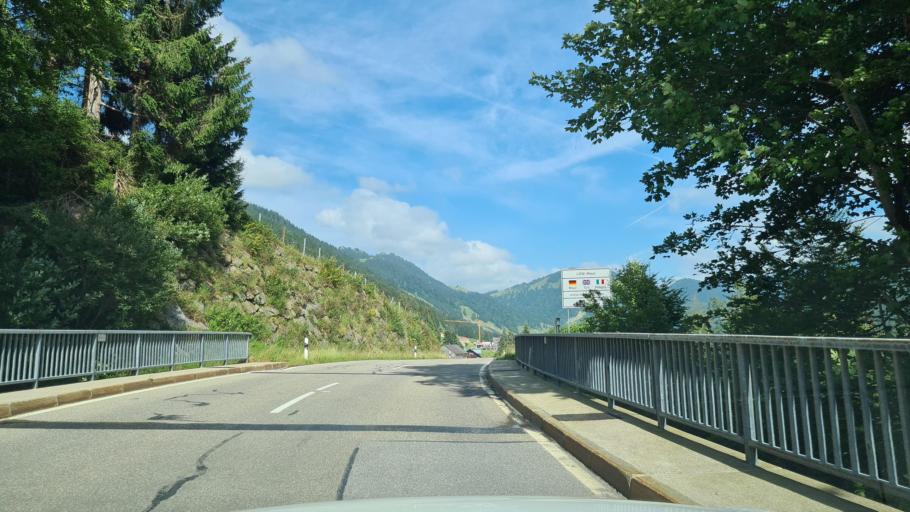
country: DE
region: Bavaria
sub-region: Swabia
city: Balderschwang
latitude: 47.4586
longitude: 10.0690
